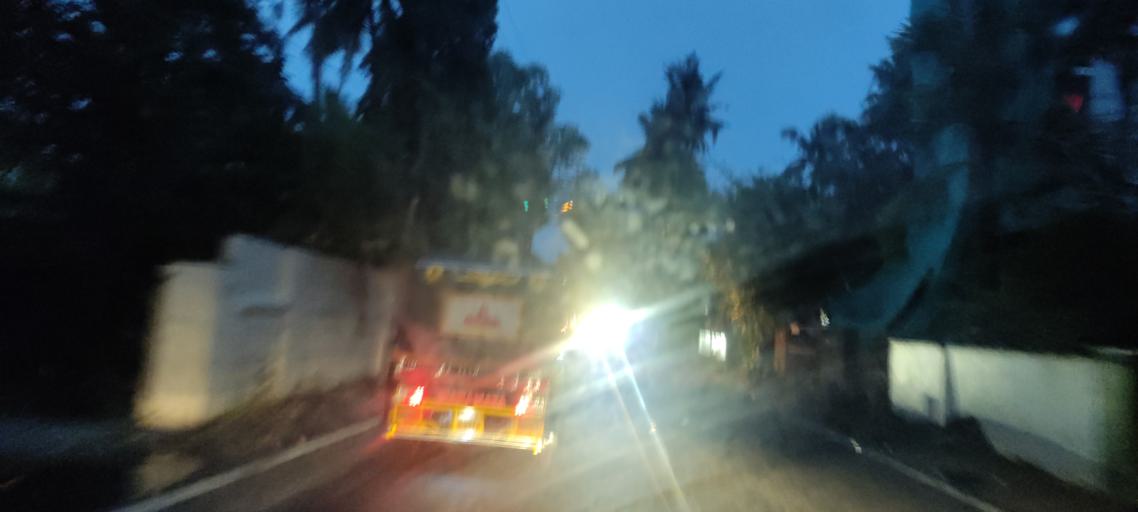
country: IN
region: Kerala
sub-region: Ernakulam
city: Cochin
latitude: 9.8991
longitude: 76.2953
